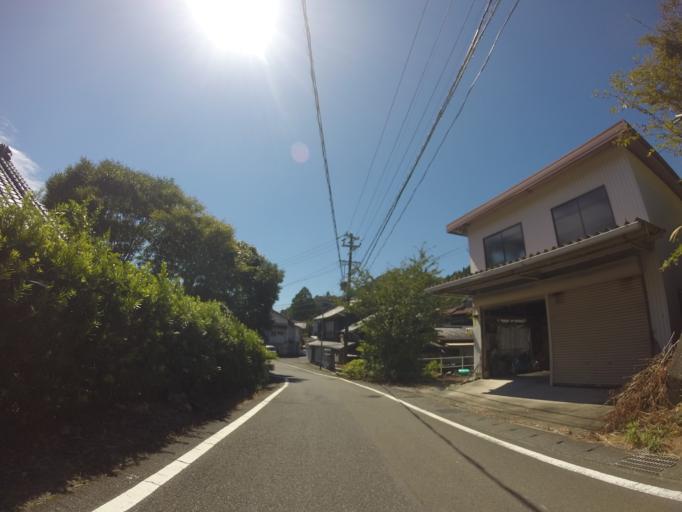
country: JP
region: Shizuoka
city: Fujieda
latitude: 34.9682
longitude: 138.2125
